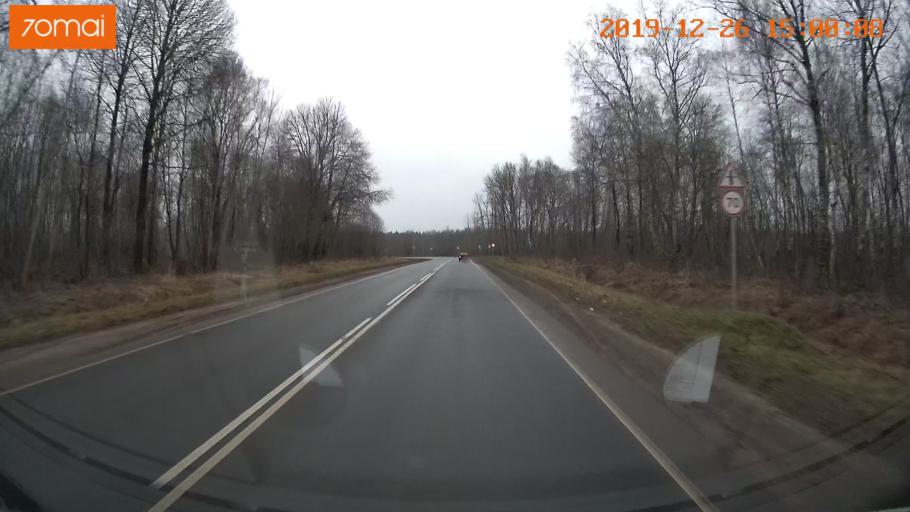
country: RU
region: Jaroslavl
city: Rybinsk
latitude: 58.2494
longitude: 38.8493
